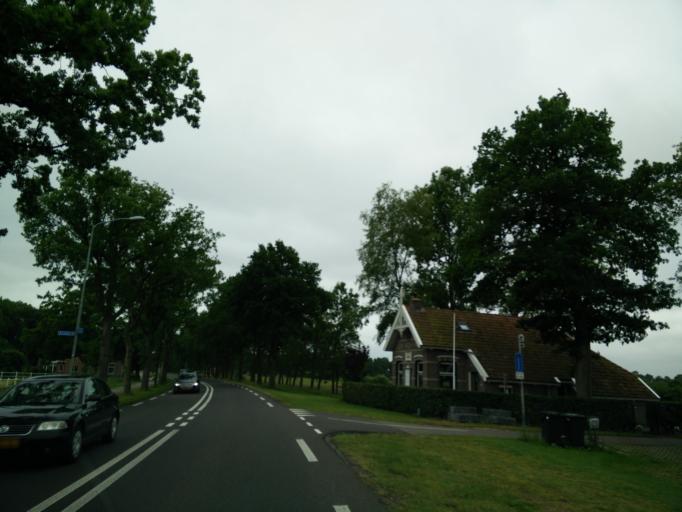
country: NL
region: Groningen
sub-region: Gemeente Groningen
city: Groningen
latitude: 53.1658
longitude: 6.4960
